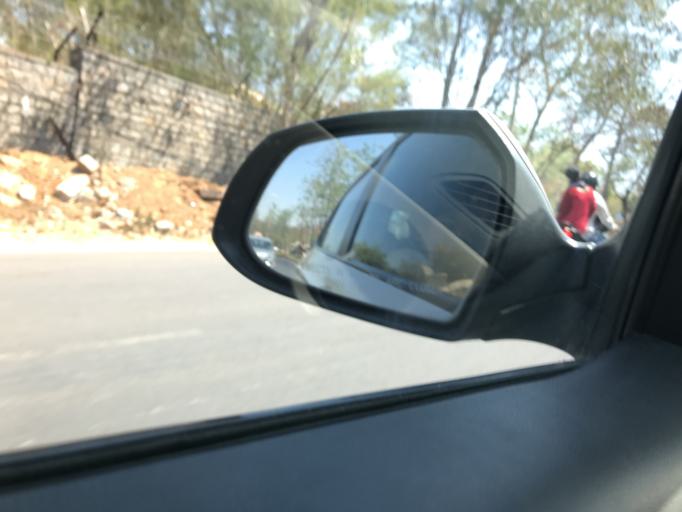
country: IN
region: Telangana
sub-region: Medak
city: Serilingampalle
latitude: 17.4579
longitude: 78.3374
